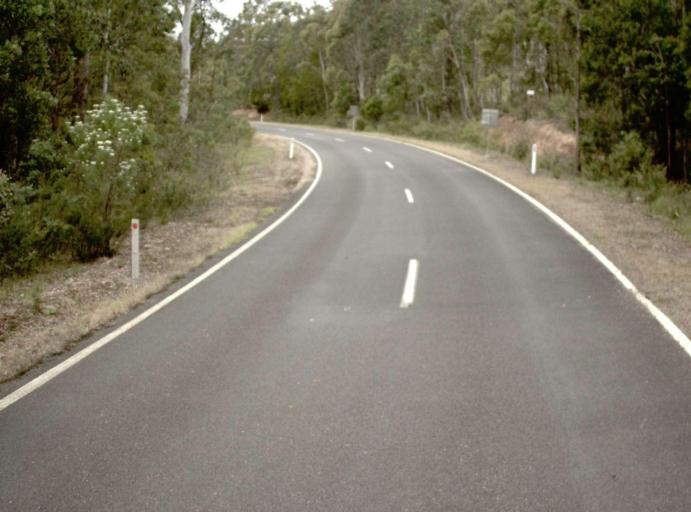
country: AU
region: Victoria
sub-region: East Gippsland
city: Bairnsdale
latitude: -37.6348
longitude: 147.2264
